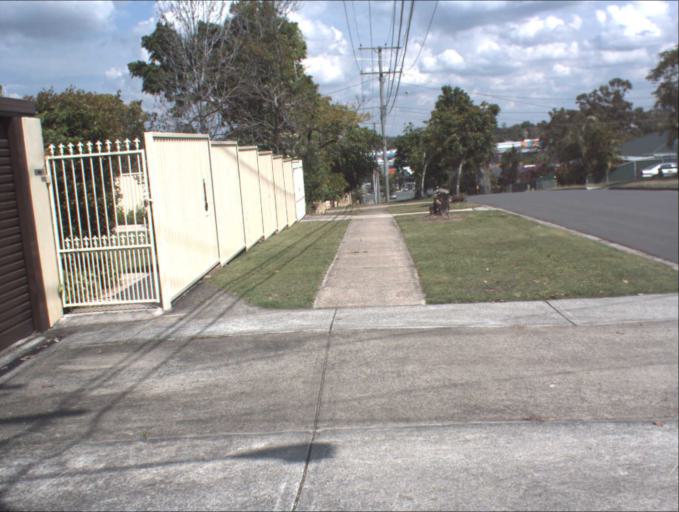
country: AU
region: Queensland
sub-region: Brisbane
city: Sunnybank Hills
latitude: -27.6596
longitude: 153.0463
